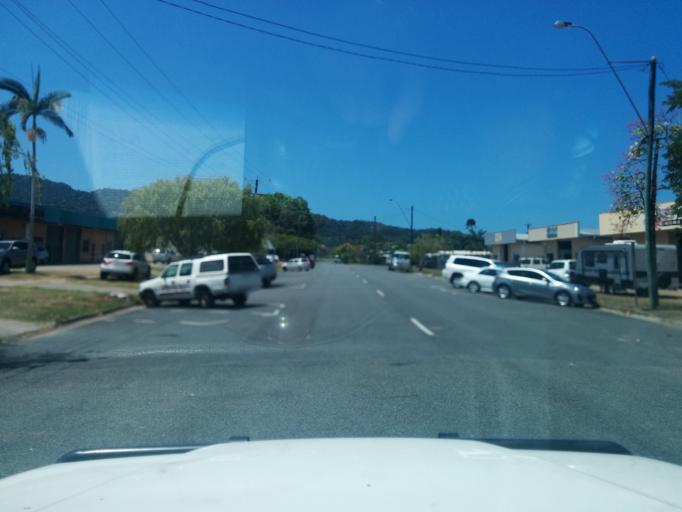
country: AU
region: Queensland
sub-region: Cairns
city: Cairns
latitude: -16.9153
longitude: 145.7451
